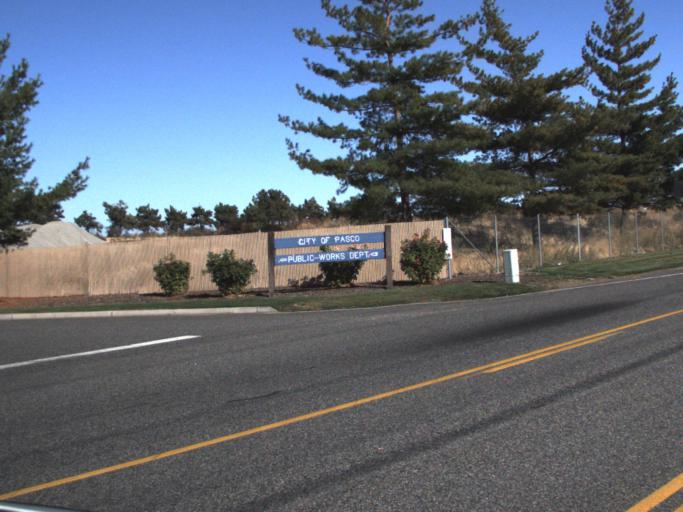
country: US
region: Washington
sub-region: Franklin County
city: Pasco
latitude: 46.2203
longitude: -119.0867
